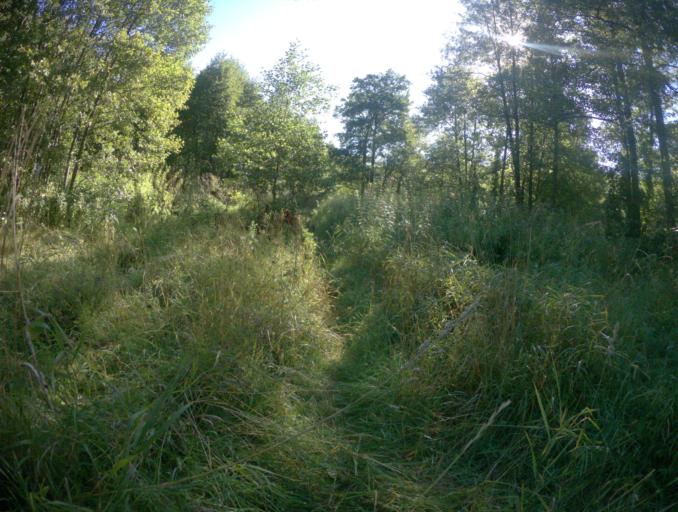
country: RU
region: Vladimir
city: Krasnaya Gorbatka
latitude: 55.7893
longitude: 41.6617
